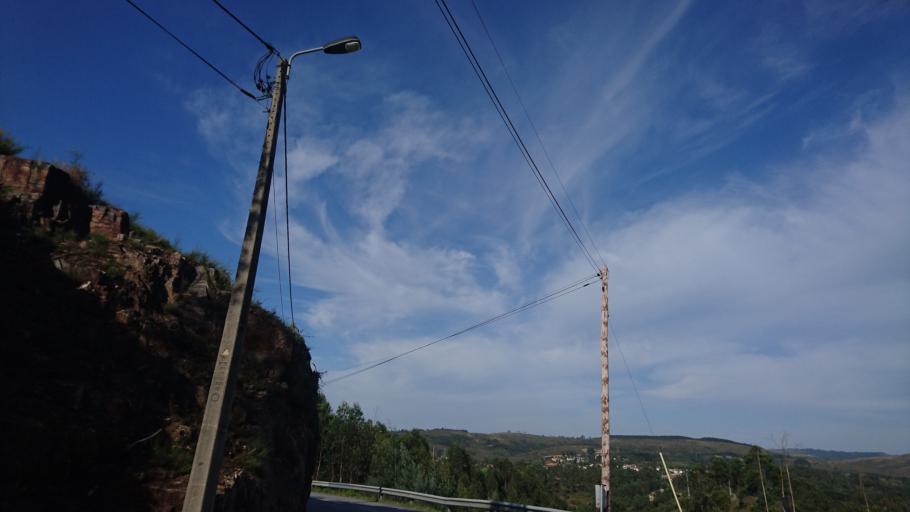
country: PT
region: Porto
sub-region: Paredes
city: Recarei
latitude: 41.1282
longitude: -8.4300
